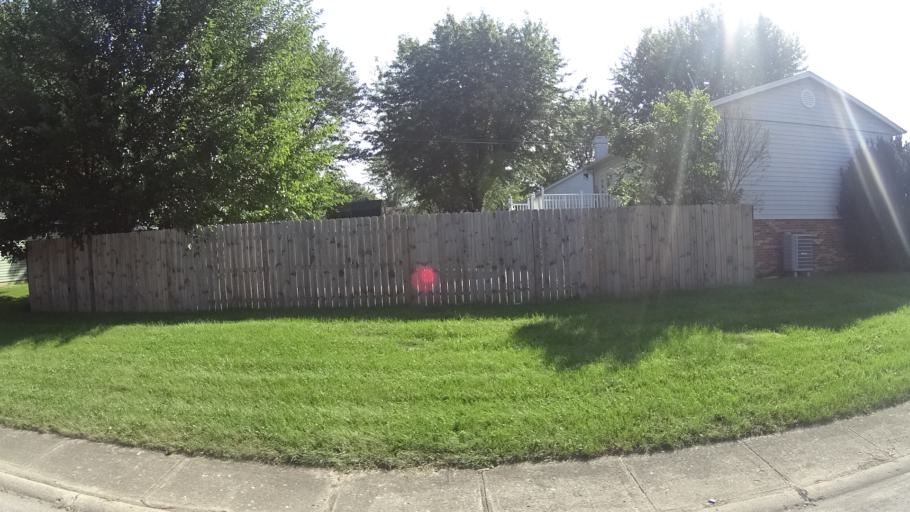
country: US
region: Indiana
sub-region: Madison County
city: Lapel
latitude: 40.0716
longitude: -85.8461
